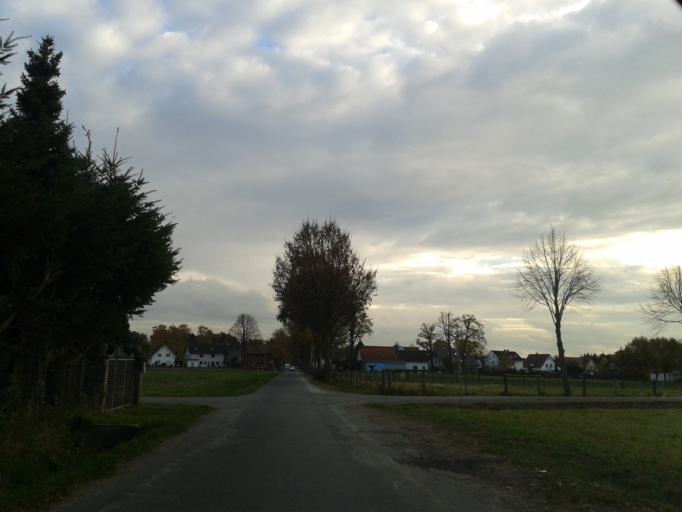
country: DE
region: North Rhine-Westphalia
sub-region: Regierungsbezirk Detmold
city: Paderborn
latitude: 51.7603
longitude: 8.7412
